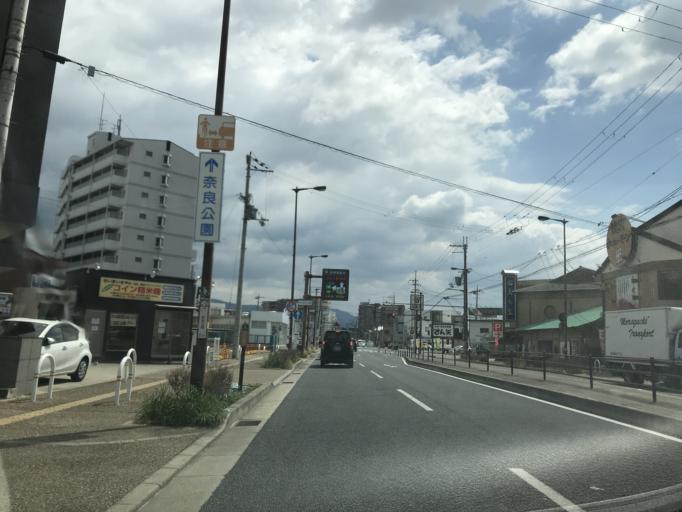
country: JP
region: Nara
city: Nara-shi
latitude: 34.6803
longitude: 135.8111
